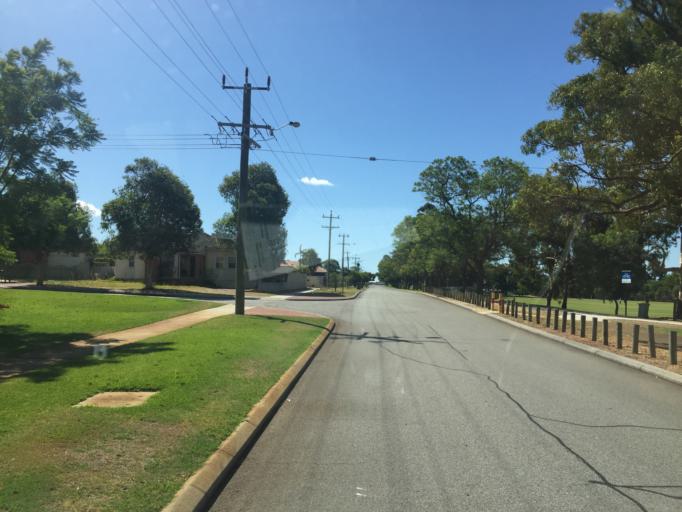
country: AU
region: Western Australia
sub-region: Belmont
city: Redcliffe
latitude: -31.9362
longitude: 115.9414
